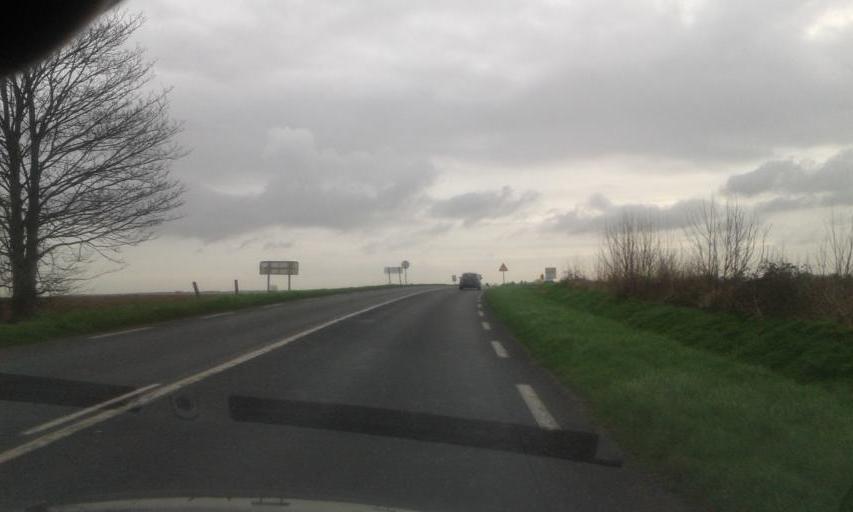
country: FR
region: Haute-Normandie
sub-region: Departement de l'Eure
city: Pont-Saint-Pierre
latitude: 49.3884
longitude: 1.2884
